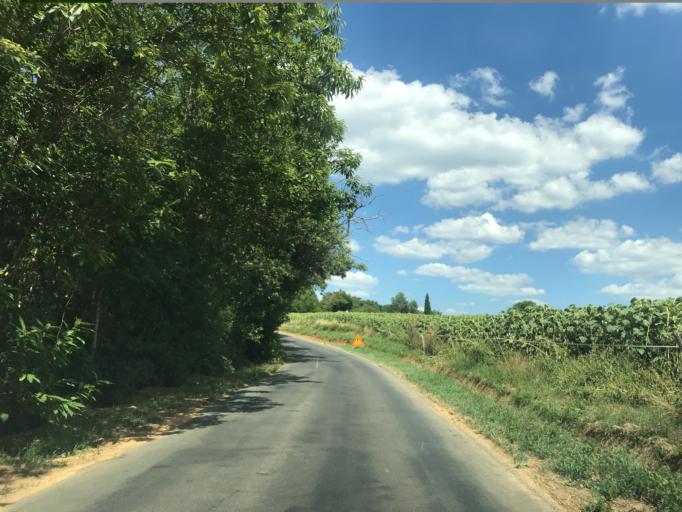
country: FR
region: Aquitaine
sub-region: Departement de la Dordogne
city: Domme
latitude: 44.8414
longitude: 1.1993
